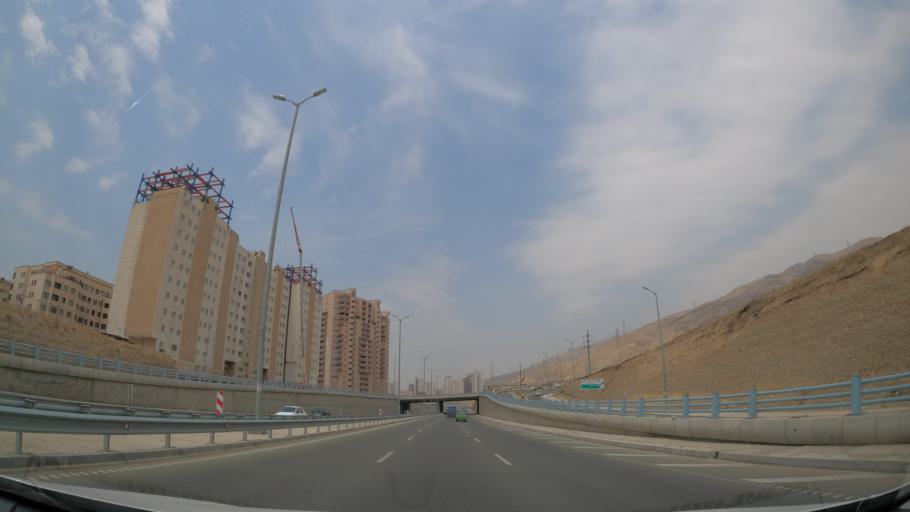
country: IR
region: Tehran
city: Shahr-e Qods
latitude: 35.7515
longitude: 51.1562
